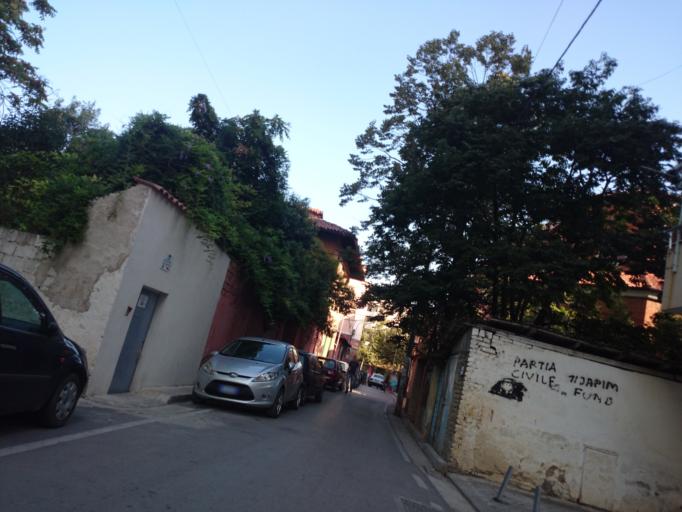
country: AL
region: Tirane
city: Tirana
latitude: 41.3267
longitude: 19.8095
